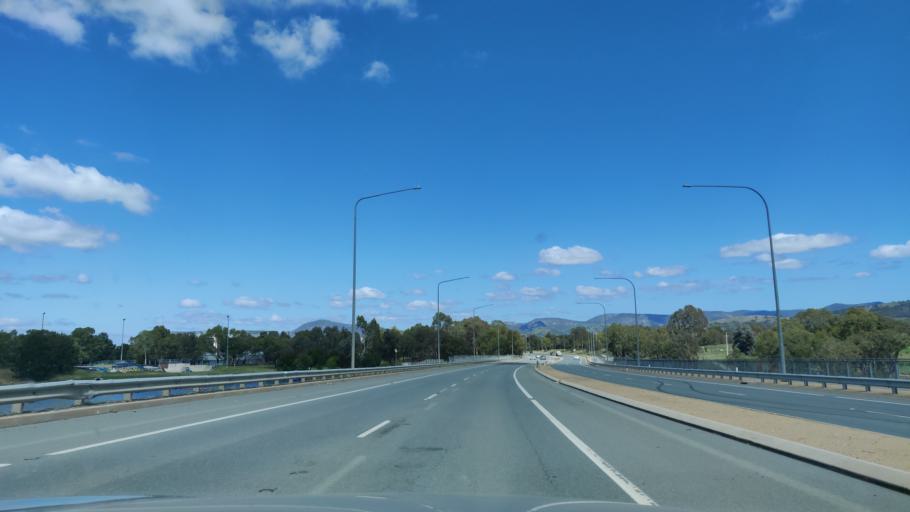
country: AU
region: Australian Capital Territory
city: Macarthur
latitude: -35.4074
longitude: 149.0638
